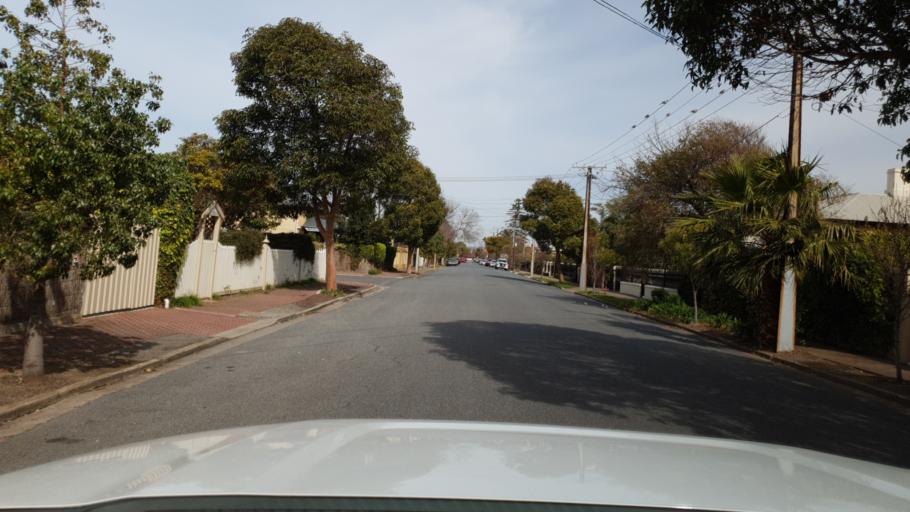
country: AU
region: South Australia
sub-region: Adelaide
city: Glenelg
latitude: -34.9859
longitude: 138.5152
